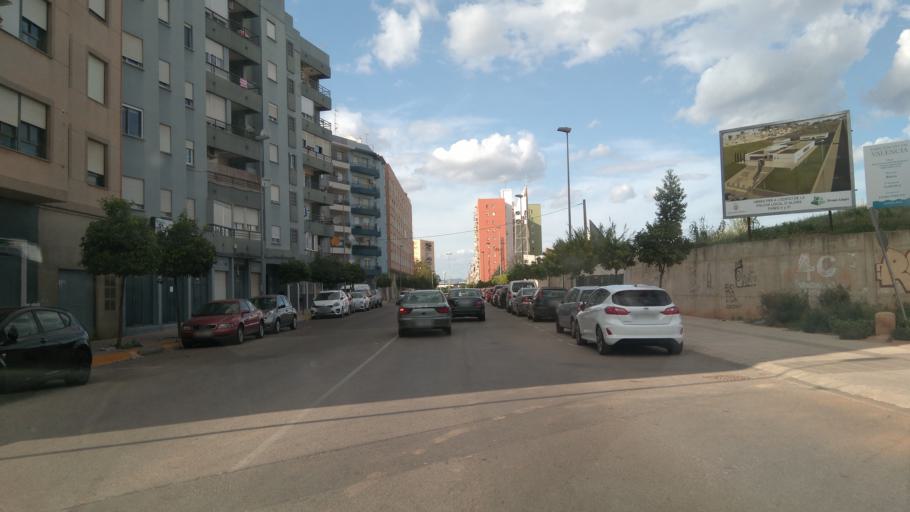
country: ES
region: Valencia
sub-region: Provincia de Valencia
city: Alzira
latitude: 39.1550
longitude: -0.4271
